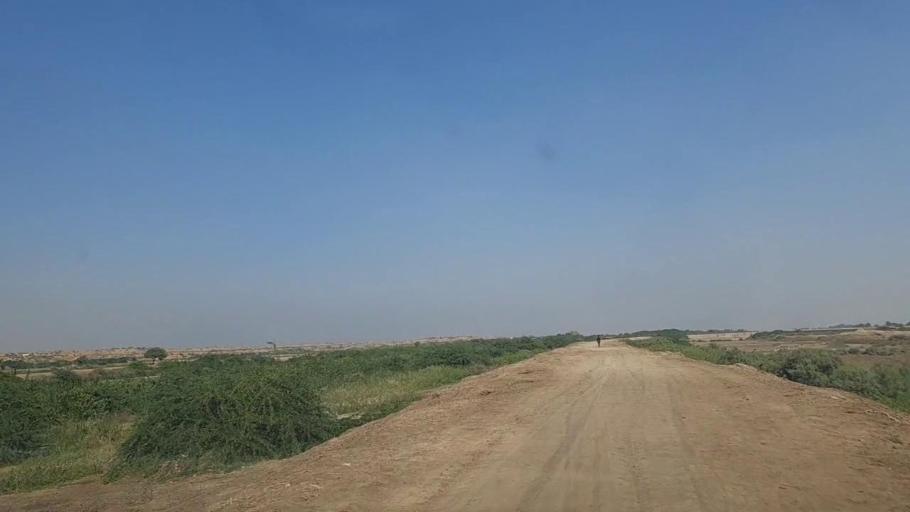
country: PK
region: Sindh
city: Thatta
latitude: 24.8443
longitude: 68.0231
